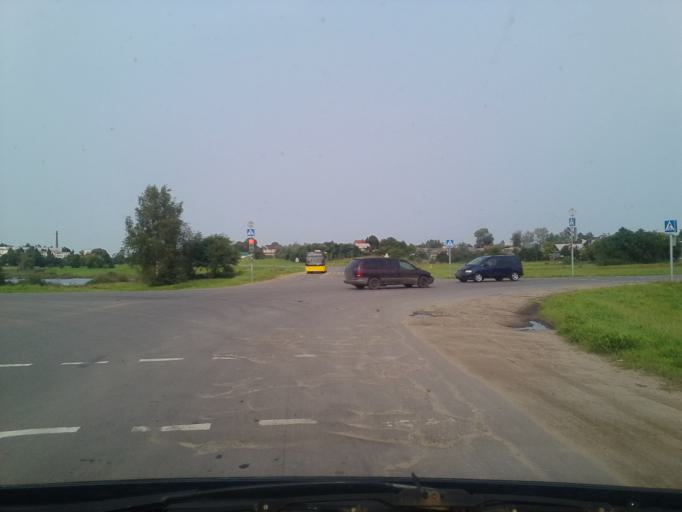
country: BY
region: Minsk
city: Hatava
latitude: 53.7765
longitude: 27.6437
